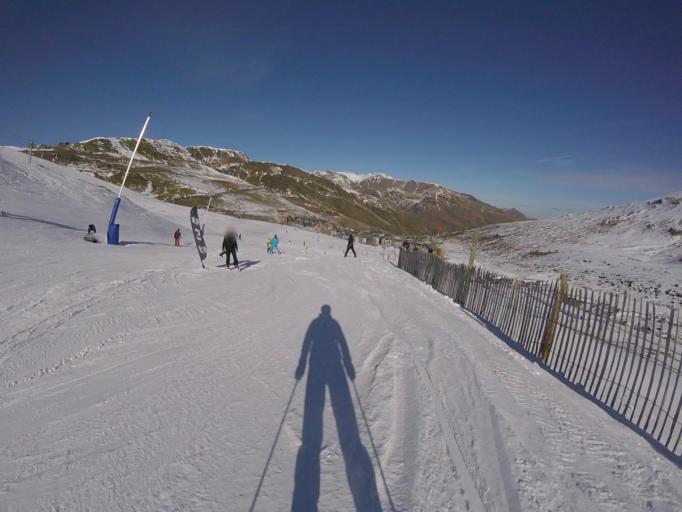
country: AD
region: Encamp
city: Pas de la Casa
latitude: 42.5337
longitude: 1.7313
